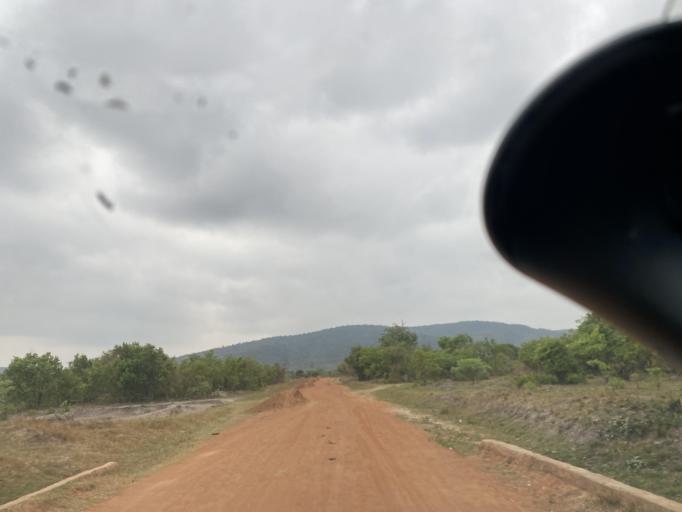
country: ZM
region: Lusaka
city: Chongwe
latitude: -15.1980
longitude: 28.7651
